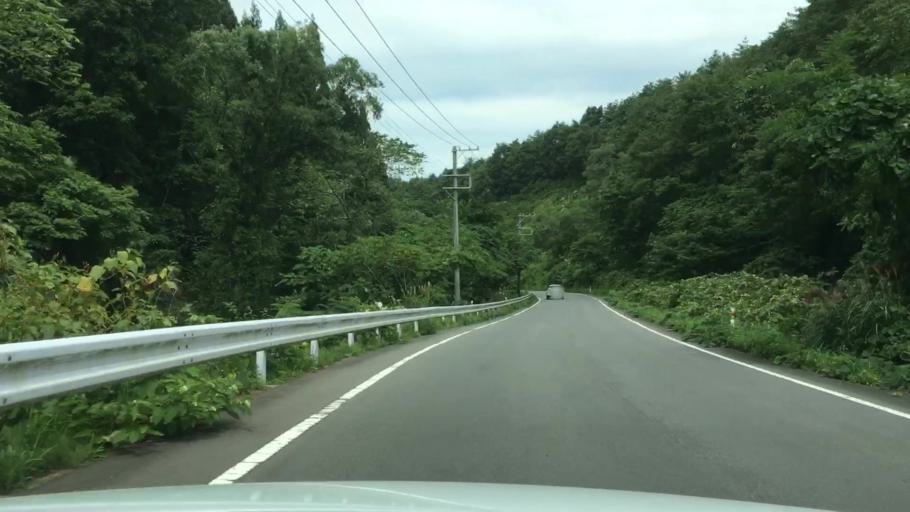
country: JP
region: Aomori
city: Shimokizukuri
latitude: 40.7271
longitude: 140.2537
